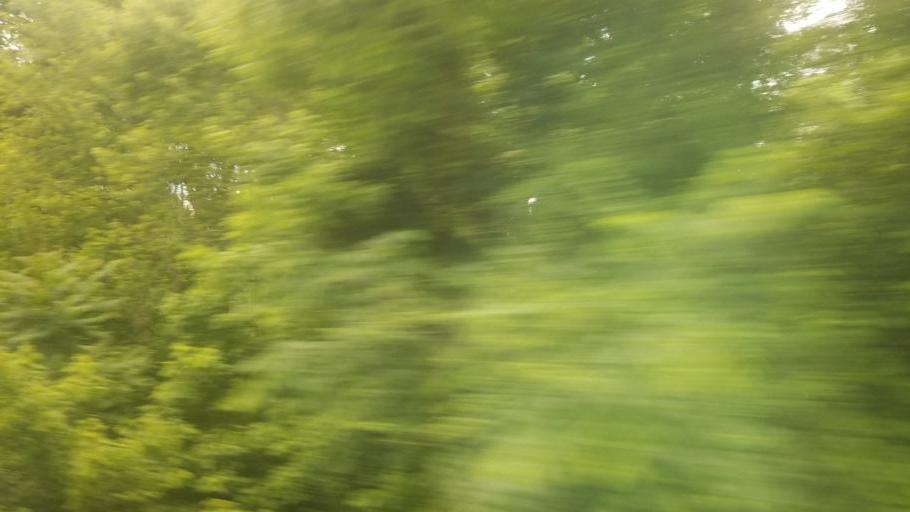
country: US
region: Maryland
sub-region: Frederick County
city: Brunswick
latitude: 39.3061
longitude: -77.6041
